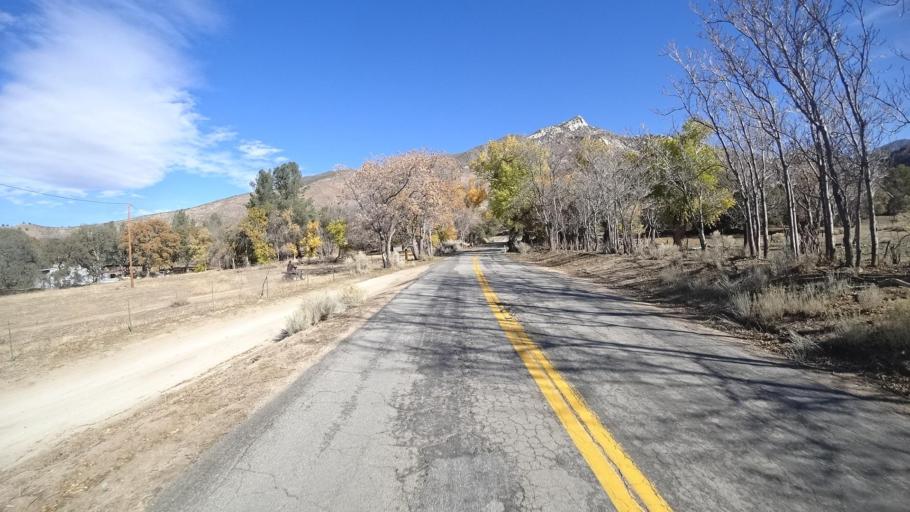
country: US
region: California
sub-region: Kern County
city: Bodfish
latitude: 35.5439
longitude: -118.5090
